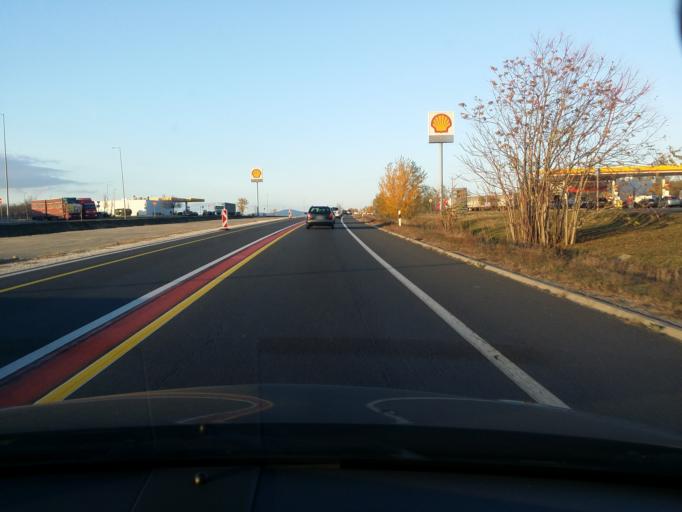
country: HU
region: Pest
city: Dunakeszi
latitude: 47.6541
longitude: 19.1596
